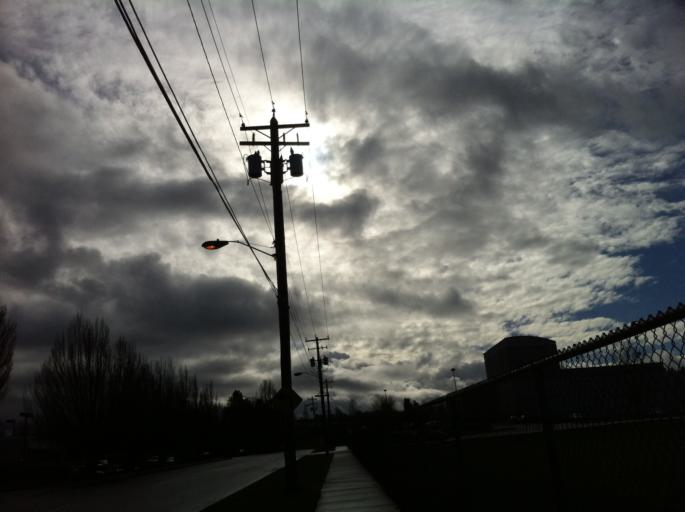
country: US
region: Oregon
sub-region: Multnomah County
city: Lents
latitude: 45.5546
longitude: -122.5383
